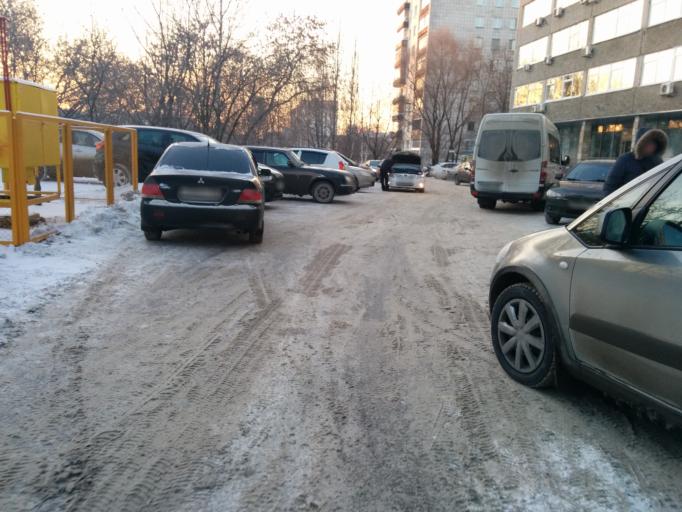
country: RU
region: Perm
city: Perm
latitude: 58.0122
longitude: 56.2241
